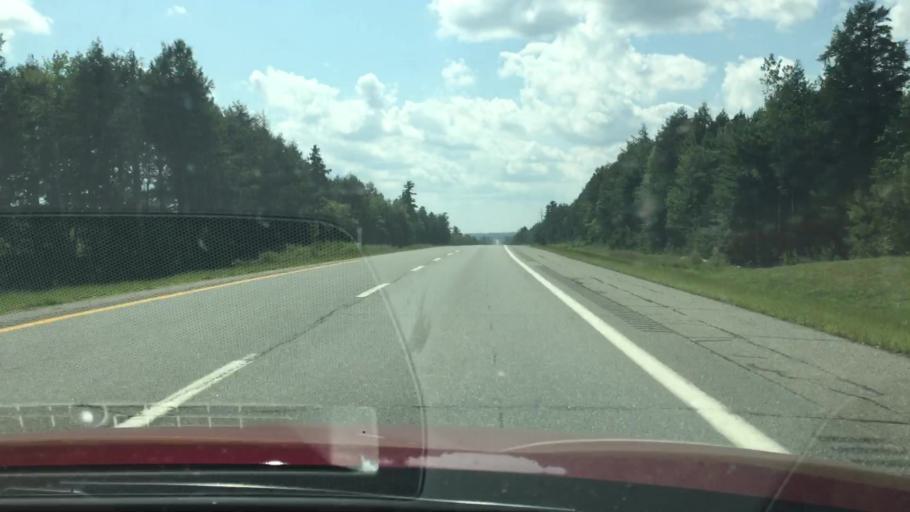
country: US
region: Maine
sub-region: Penobscot County
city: Lincoln
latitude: 45.3494
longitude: -68.6120
